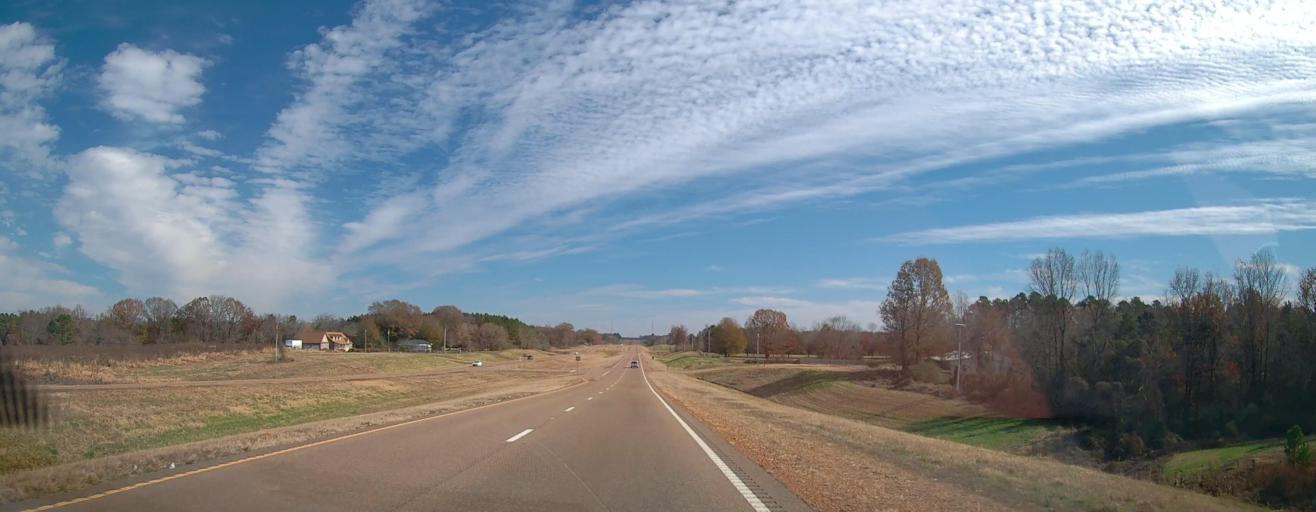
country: US
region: Mississippi
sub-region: Benton County
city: Ashland
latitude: 34.9458
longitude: -89.1795
